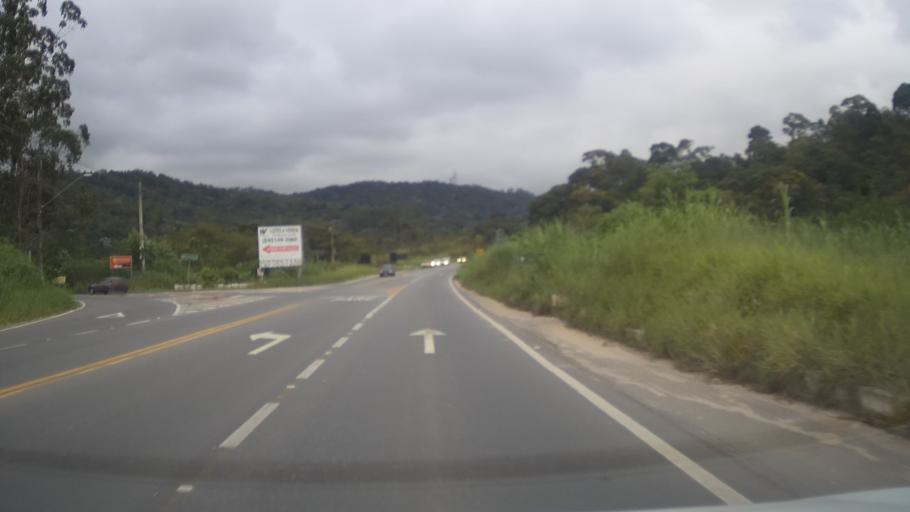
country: BR
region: Sao Paulo
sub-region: Aruja
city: Aruja
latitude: -23.3810
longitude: -46.4355
